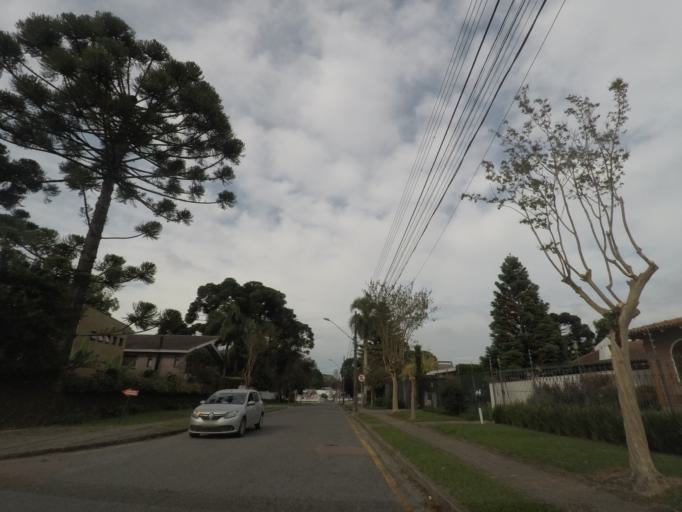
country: BR
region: Parana
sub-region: Curitiba
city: Curitiba
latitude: -25.4096
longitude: -49.2742
